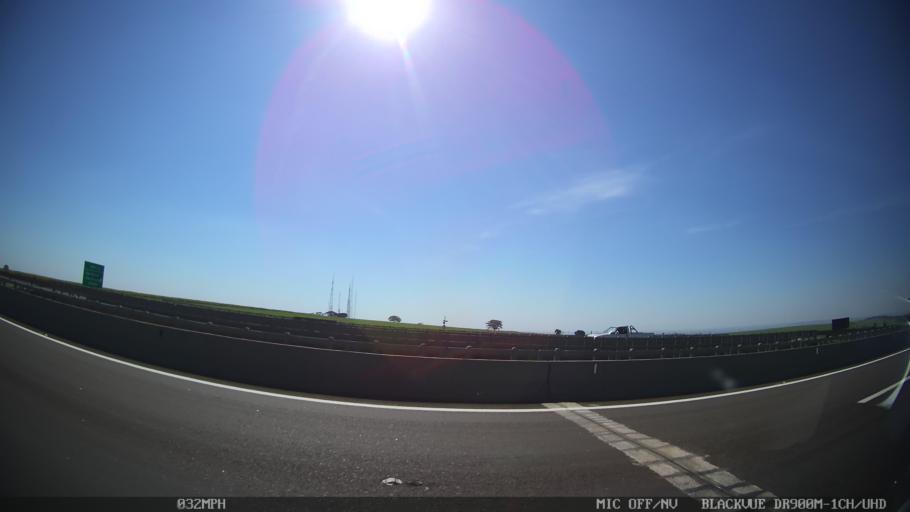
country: BR
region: Sao Paulo
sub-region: Ribeirao Preto
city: Ribeirao Preto
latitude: -21.1667
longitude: -47.8998
